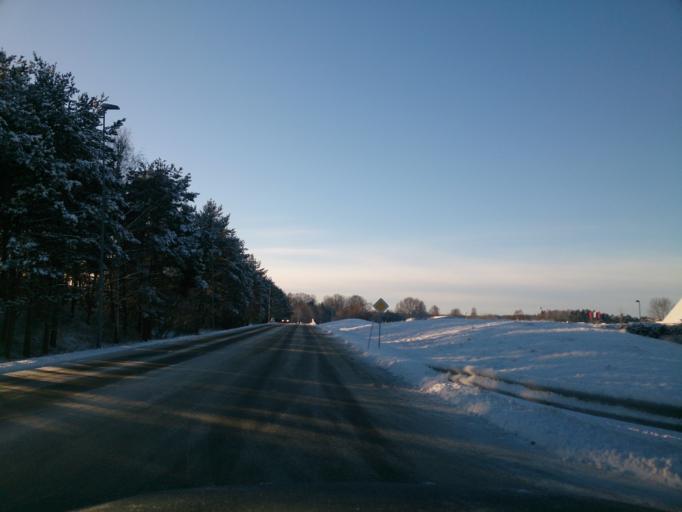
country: SE
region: OEstergoetland
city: Lindo
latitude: 58.5717
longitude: 16.2348
